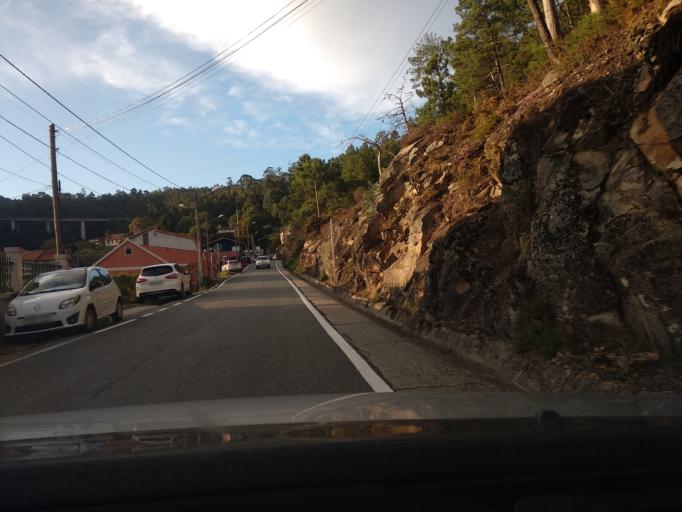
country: ES
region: Galicia
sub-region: Provincia de Pontevedra
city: Redondela
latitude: 42.2935
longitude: -8.6748
